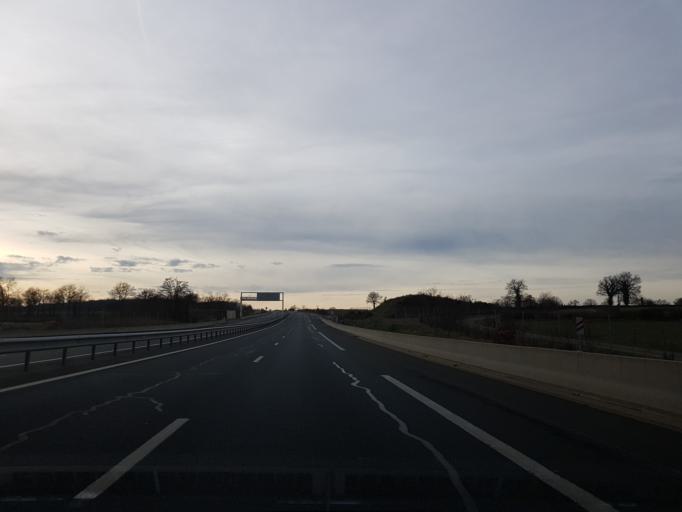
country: FR
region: Auvergne
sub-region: Departement de l'Allier
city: Desertines
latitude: 46.3751
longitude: 2.6699
